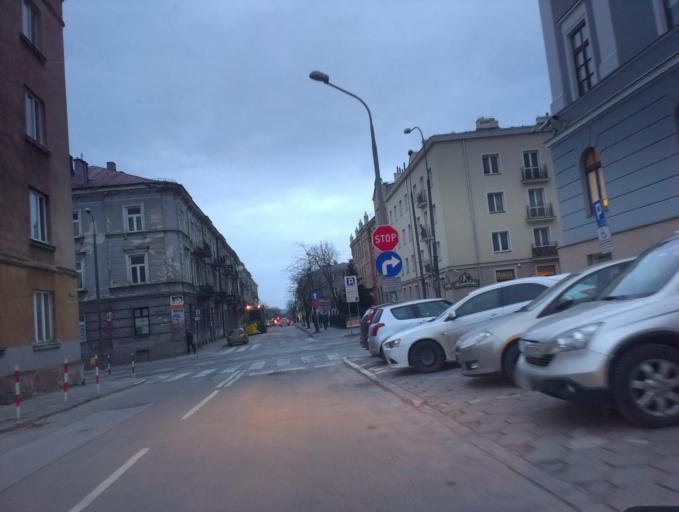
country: PL
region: Swietokrzyskie
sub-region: Powiat kielecki
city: Kielce
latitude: 50.8655
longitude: 20.6337
